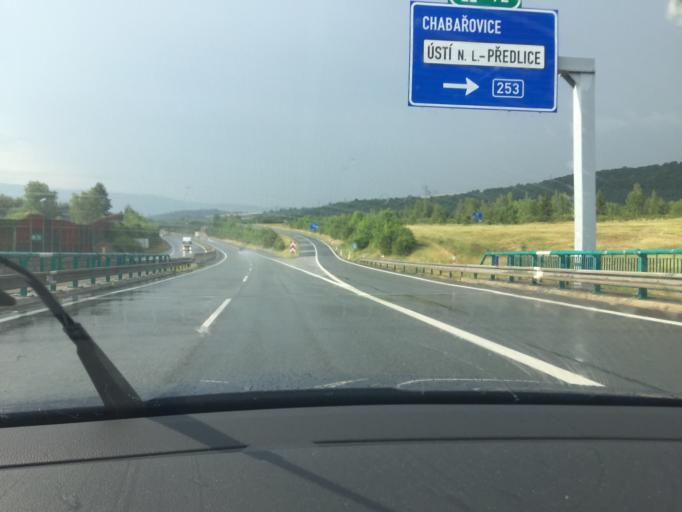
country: CZ
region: Ustecky
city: Trmice
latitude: 50.6628
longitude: 13.9794
